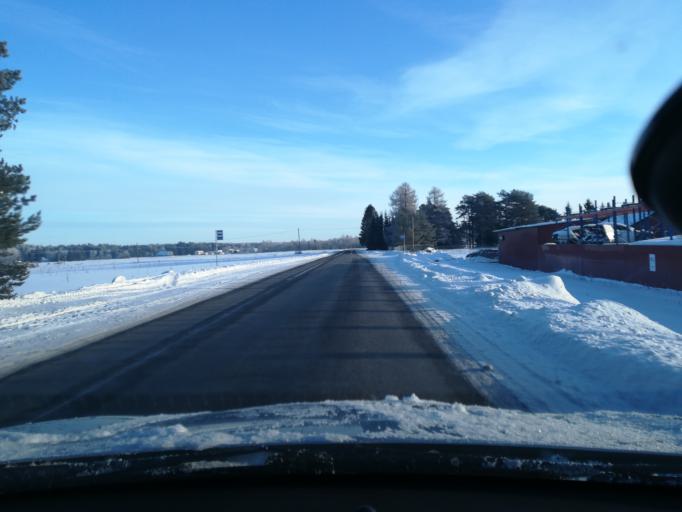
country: EE
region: Harju
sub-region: Keila linn
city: Keila
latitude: 59.3813
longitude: 24.4447
